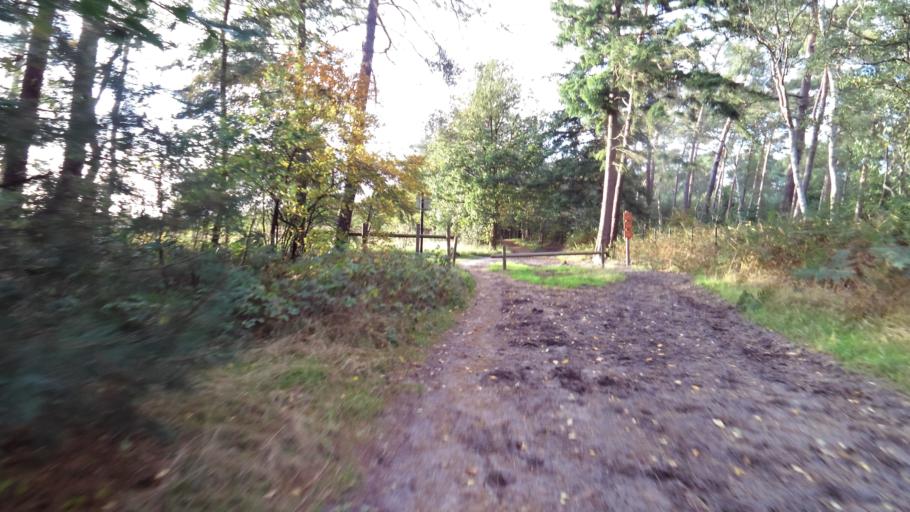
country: NL
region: Utrecht
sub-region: Gemeente Soest
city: Soest
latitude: 52.1876
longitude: 5.2556
